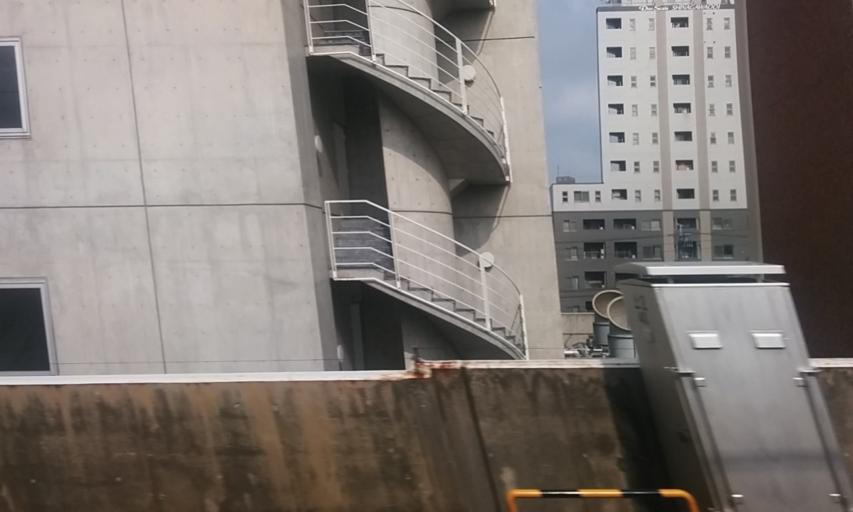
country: JP
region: Kanagawa
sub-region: Kawasaki-shi
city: Kawasaki
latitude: 35.5950
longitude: 139.7373
